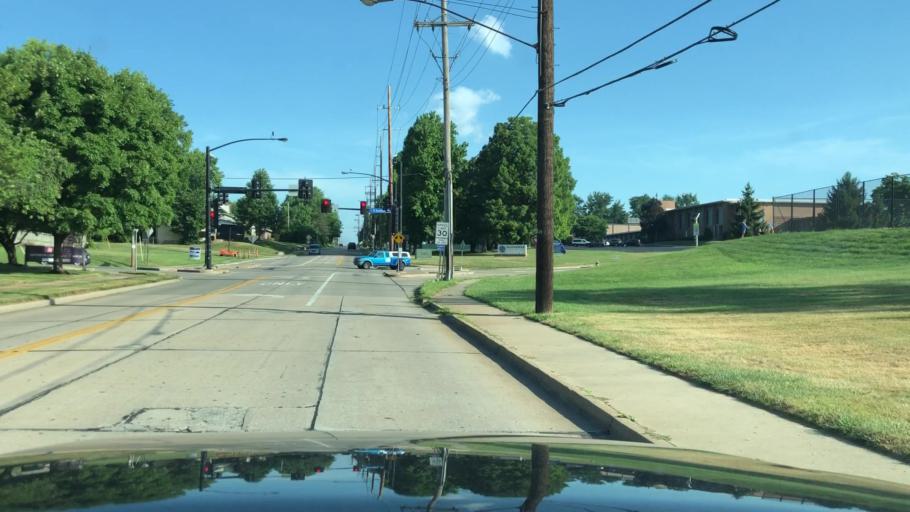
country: US
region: Missouri
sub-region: Saint Charles County
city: Saint Charles
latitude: 38.7954
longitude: -90.4997
